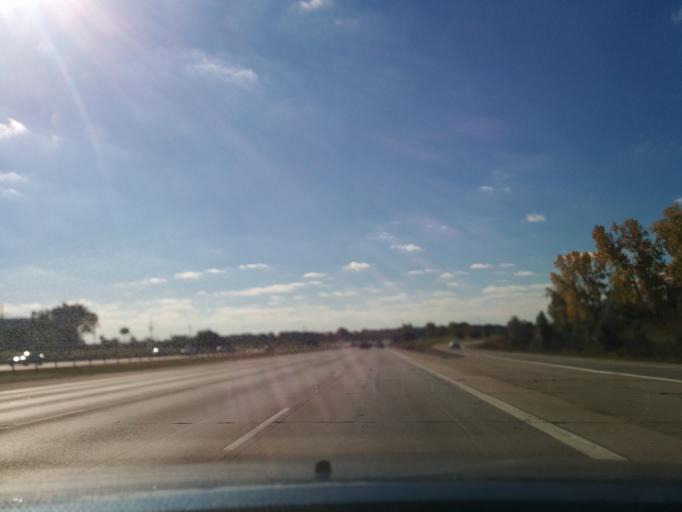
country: US
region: Michigan
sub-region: Wayne County
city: Northville
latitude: 42.4160
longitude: -83.4243
